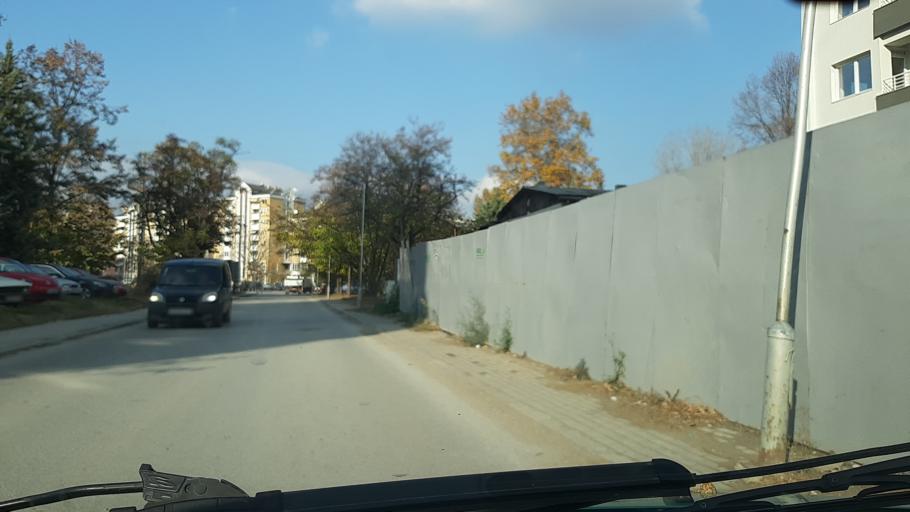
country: MK
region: Karpos
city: Skopje
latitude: 41.9858
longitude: 21.4526
